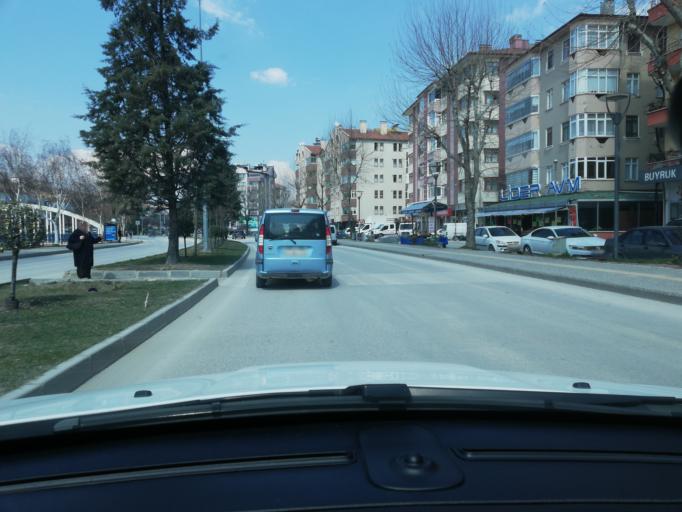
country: TR
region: Kastamonu
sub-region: Cide
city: Kastamonu
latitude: 41.3935
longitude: 33.7820
